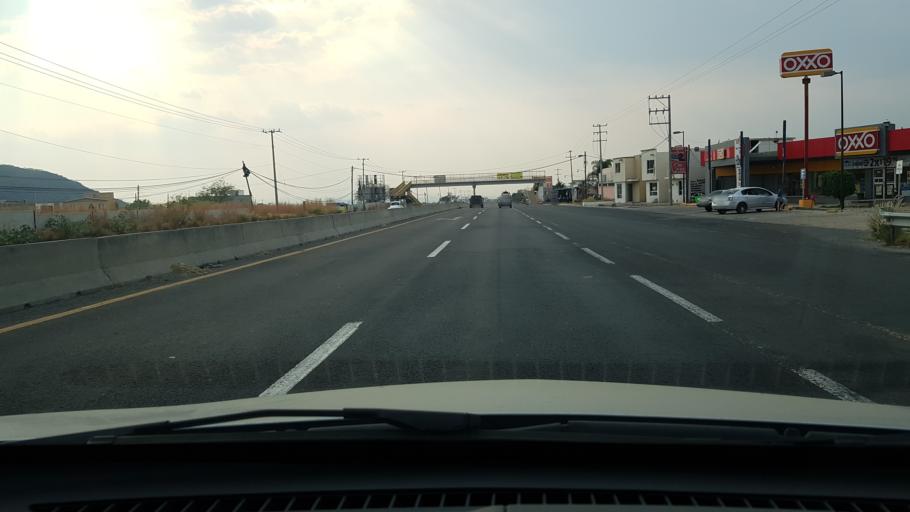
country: MX
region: Morelos
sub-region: Ayala
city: Unidad Habitacional Mariano Matamoros
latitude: 18.7508
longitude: -98.8515
